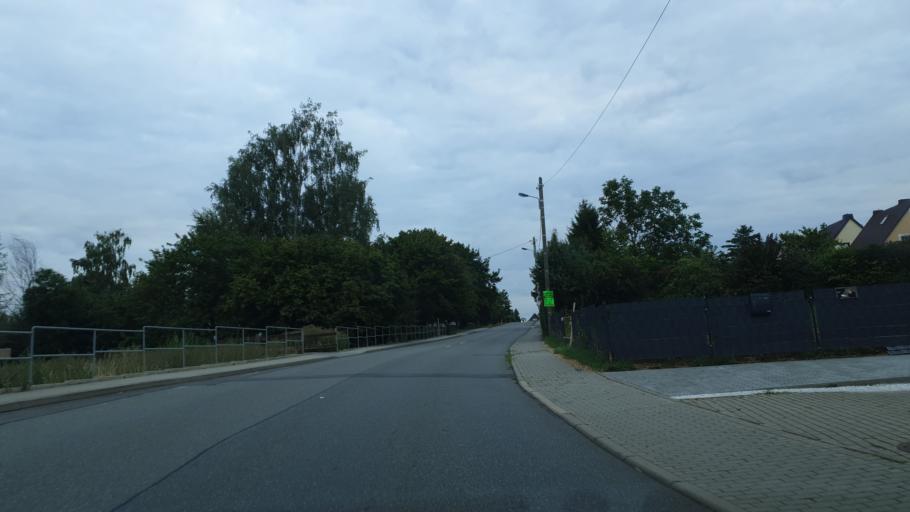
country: DE
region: Saxony
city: Callenberg
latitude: 50.8462
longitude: 12.6372
